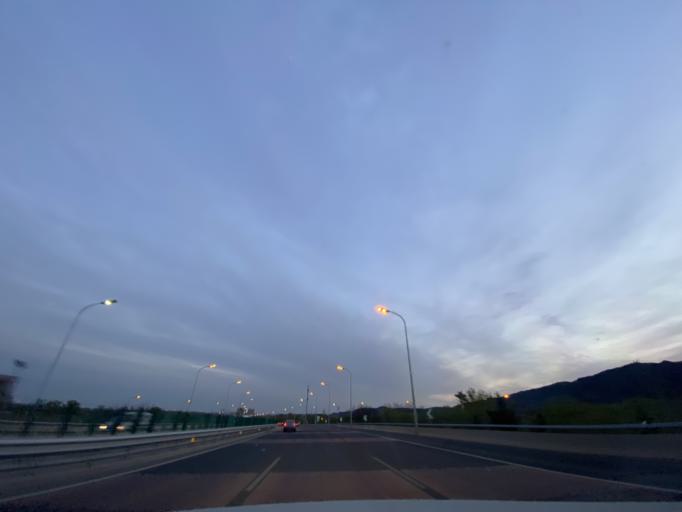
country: CN
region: Beijing
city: Xiangshan
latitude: 39.9901
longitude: 116.2154
